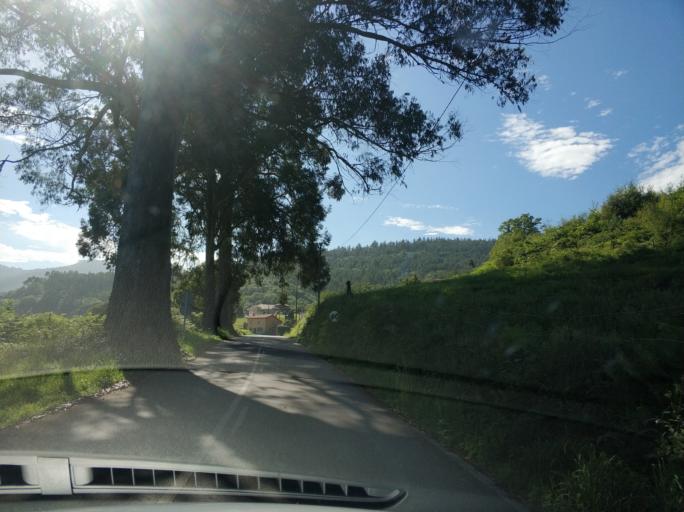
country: ES
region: Asturias
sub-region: Province of Asturias
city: Cudillero
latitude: 43.5416
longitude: -6.2330
